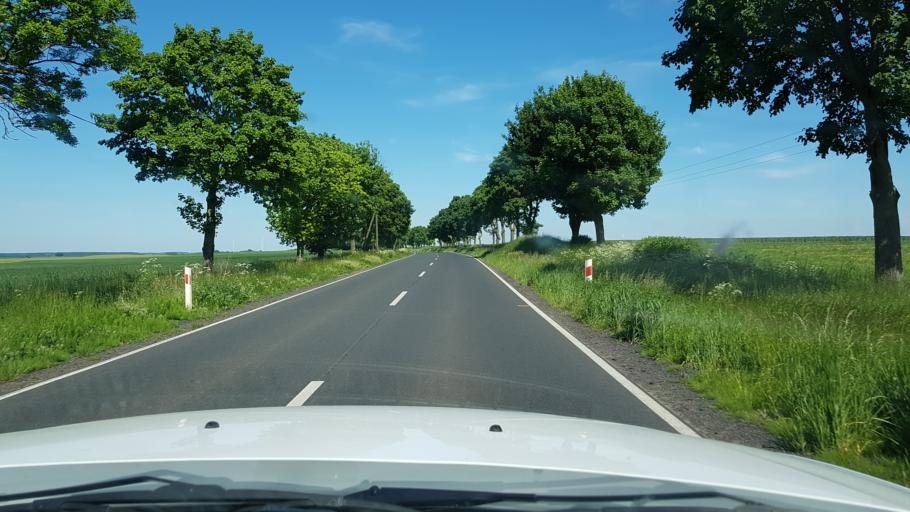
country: PL
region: West Pomeranian Voivodeship
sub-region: Powiat gryfinski
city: Banie
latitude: 53.1055
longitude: 14.6837
